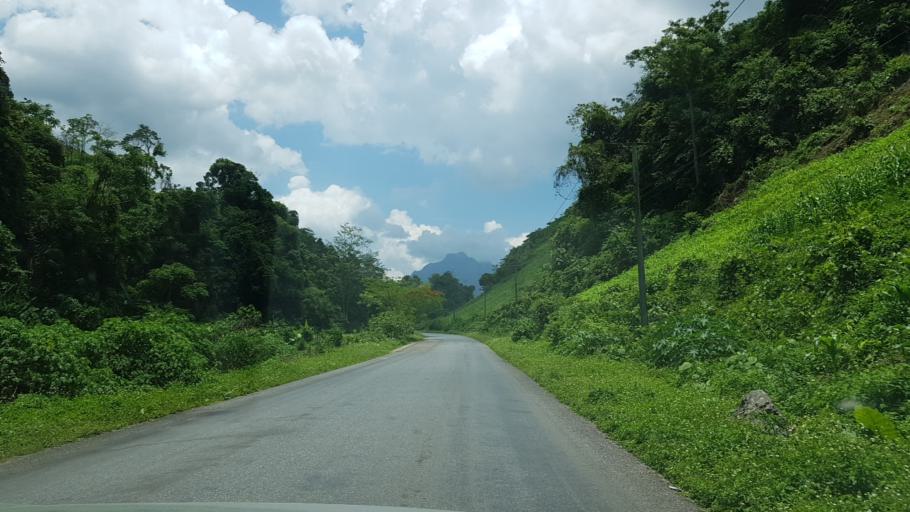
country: LA
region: Vientiane
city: Muang Kasi
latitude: 19.1390
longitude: 102.2976
